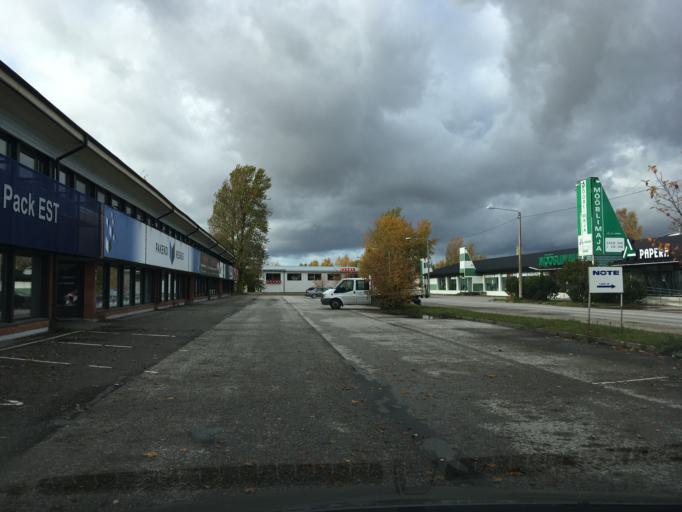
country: EE
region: Paernumaa
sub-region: Paernu linn
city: Parnu
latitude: 58.3744
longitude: 24.5496
